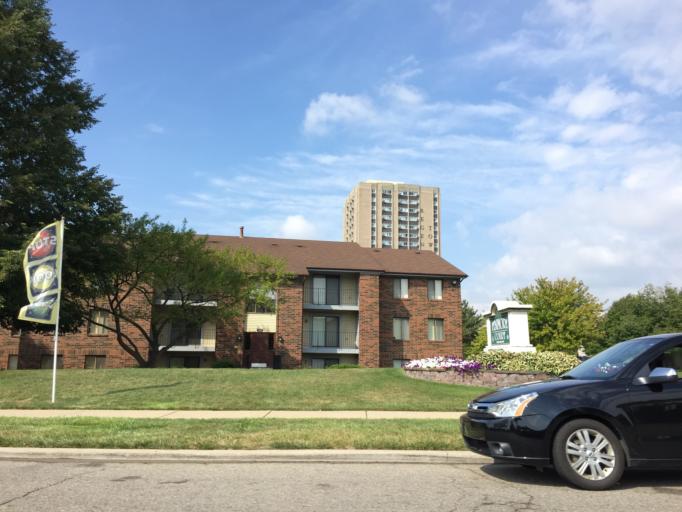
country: US
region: Michigan
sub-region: Wayne County
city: Detroit
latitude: 42.3462
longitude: -83.0259
